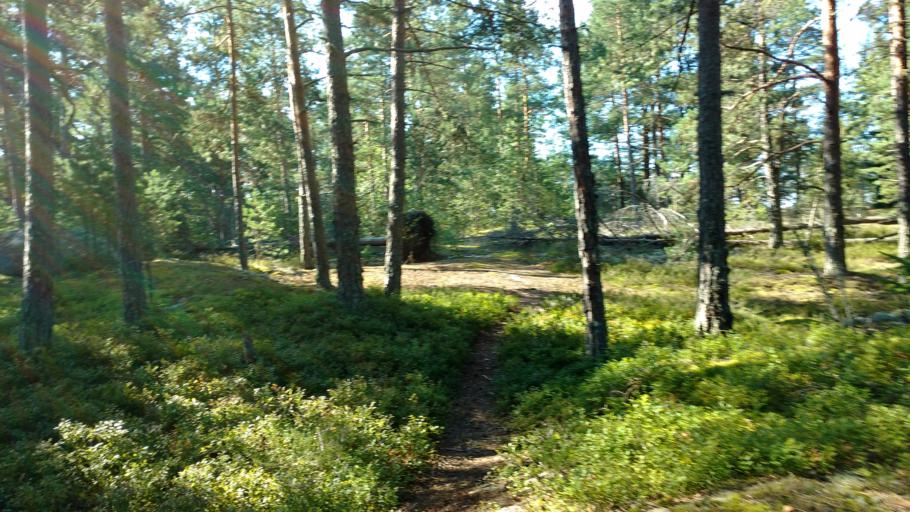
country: FI
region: Varsinais-Suomi
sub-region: Salo
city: Salo
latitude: 60.3817
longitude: 23.1702
